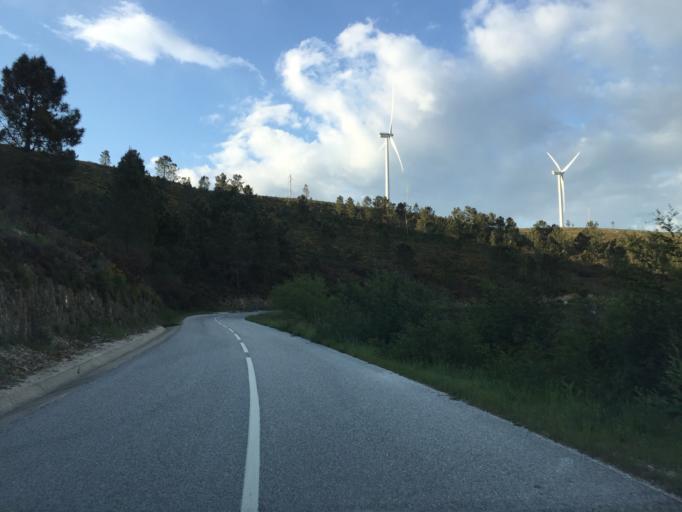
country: PT
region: Coimbra
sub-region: Pampilhosa da Serra
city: Pampilhosa da Serra
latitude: 40.1103
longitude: -8.0105
